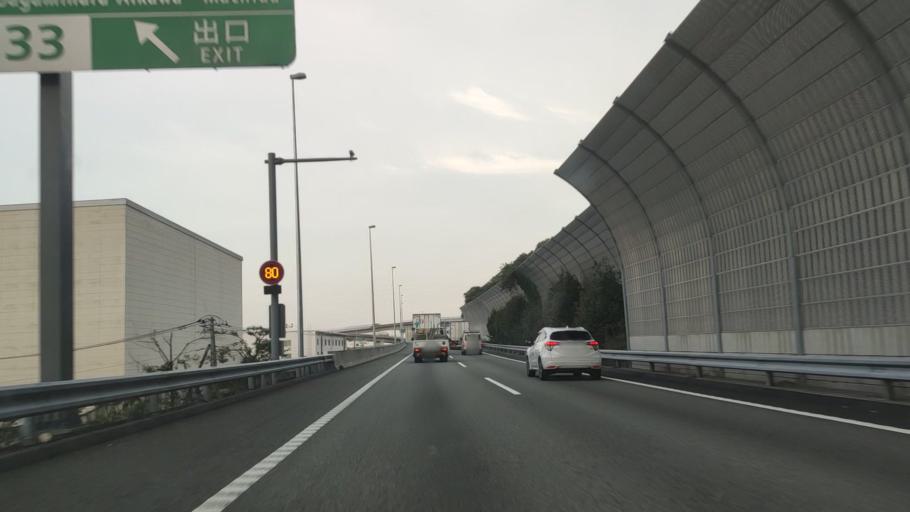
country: JP
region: Kanagawa
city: Zama
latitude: 35.5252
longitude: 139.3507
